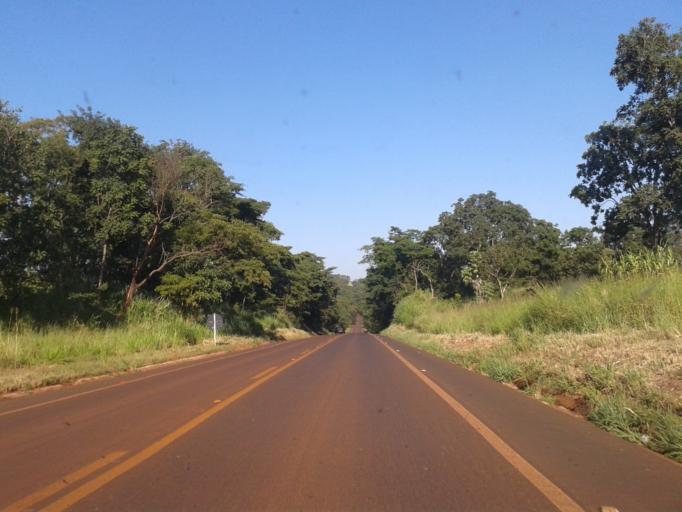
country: BR
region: Minas Gerais
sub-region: Capinopolis
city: Capinopolis
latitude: -18.6872
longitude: -49.6061
